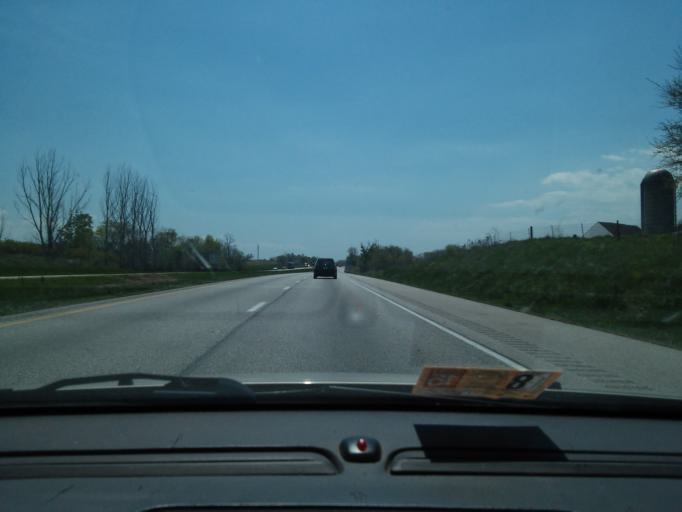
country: US
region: Pennsylvania
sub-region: Franklin County
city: Greencastle
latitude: 39.8141
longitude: -77.7036
